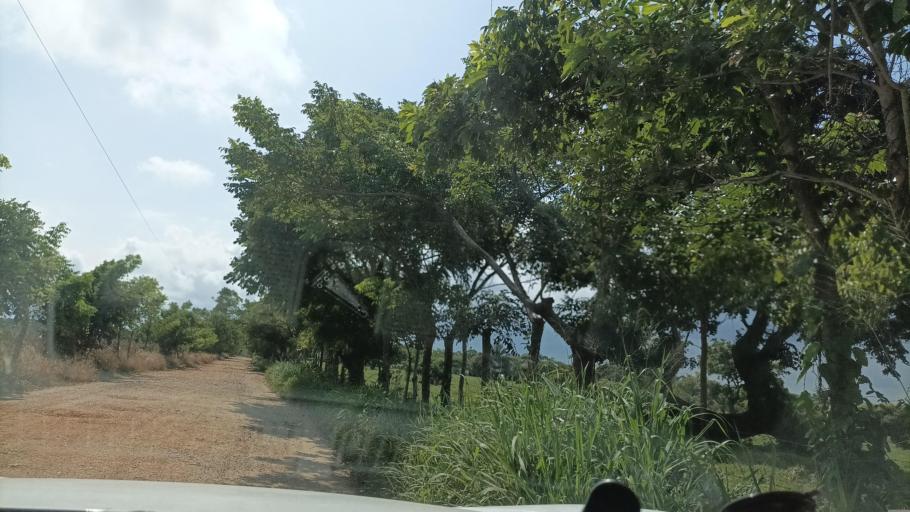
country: MX
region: Veracruz
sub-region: Chinameca
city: Chacalapa
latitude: 18.1121
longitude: -94.6642
